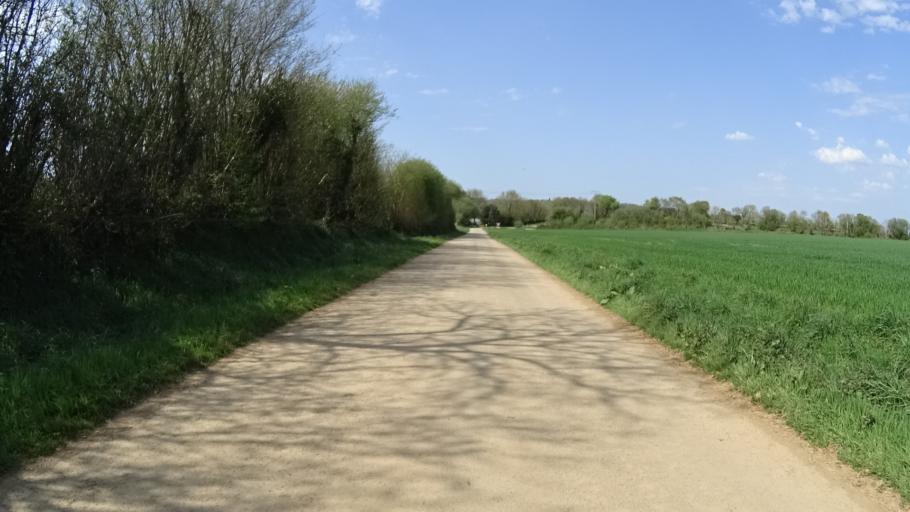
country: FR
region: Brittany
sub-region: Departement du Finistere
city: Sizun
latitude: 48.4252
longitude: -4.0901
